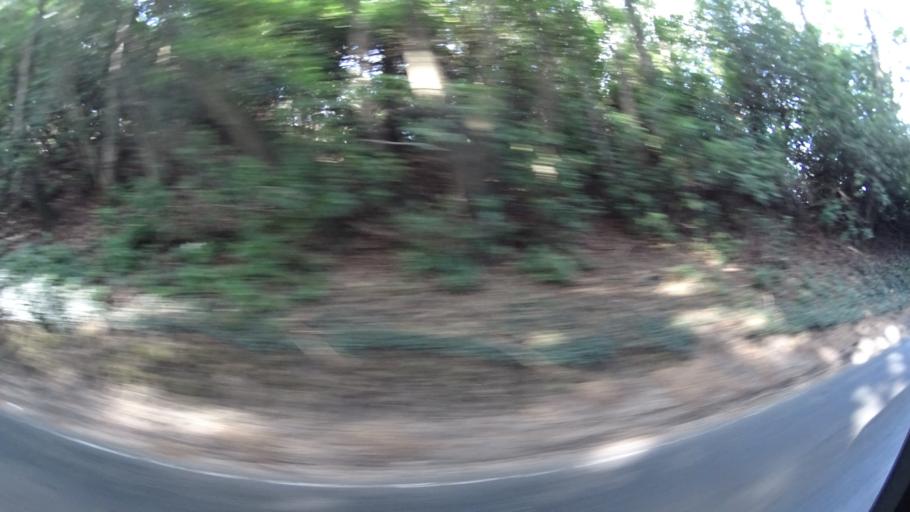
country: GB
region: England
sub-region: Dorset
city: Lytchett Matravers
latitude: 50.7547
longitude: -2.0473
